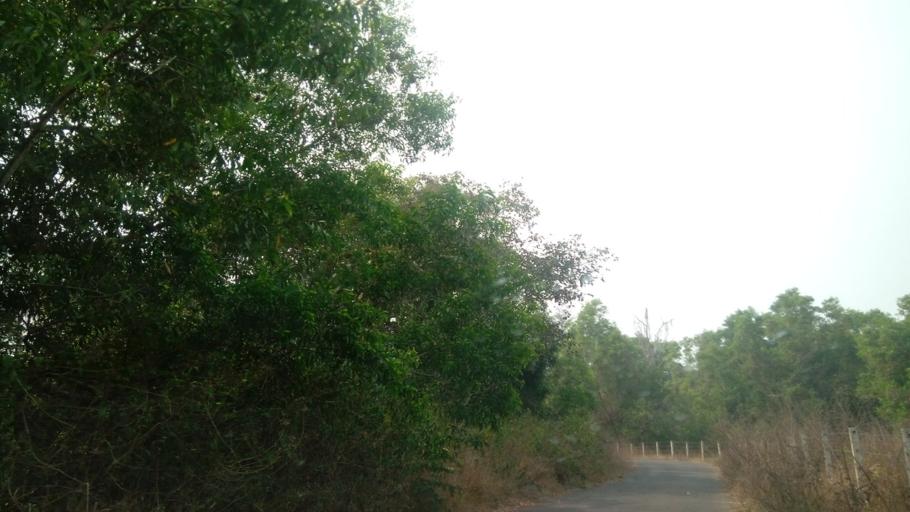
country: IN
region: Goa
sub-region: South Goa
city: Varca
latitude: 15.2185
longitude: 73.9345
